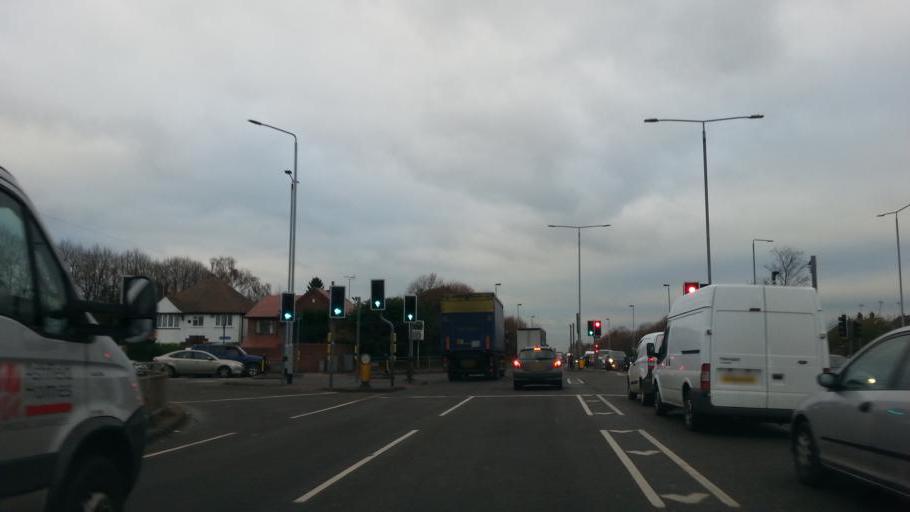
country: GB
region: England
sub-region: Nottinghamshire
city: Sutton in Ashfield
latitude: 53.1135
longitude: -1.2669
